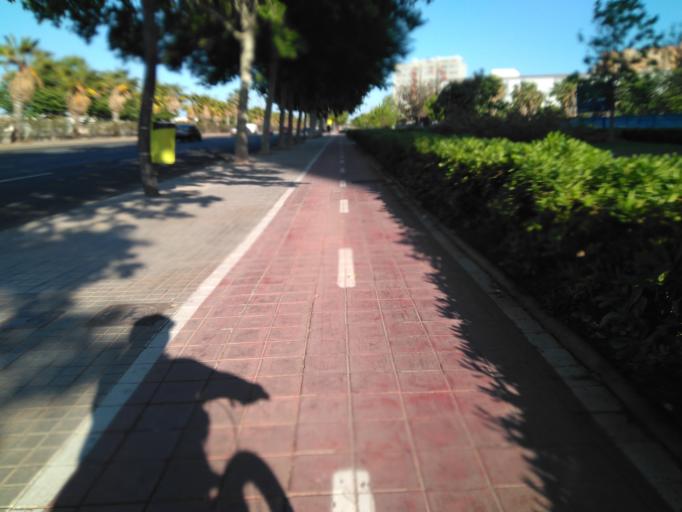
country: ES
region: Valencia
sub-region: Provincia de Valencia
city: Tavernes Blanques
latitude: 39.4955
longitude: -0.3621
